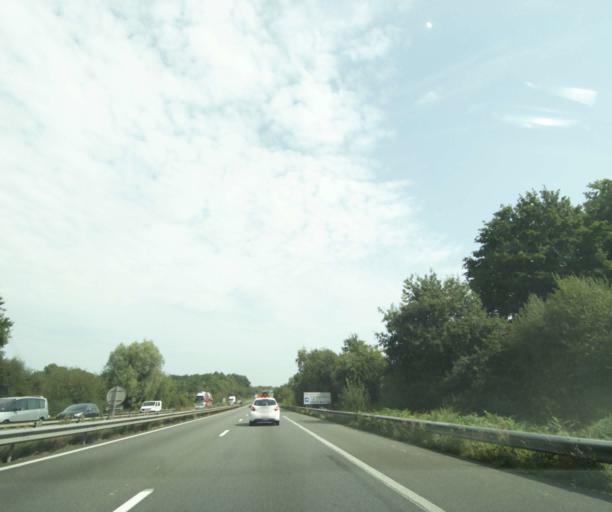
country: FR
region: Pays de la Loire
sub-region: Departement de la Loire-Atlantique
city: Les Sorinieres
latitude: 47.1672
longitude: -1.5213
